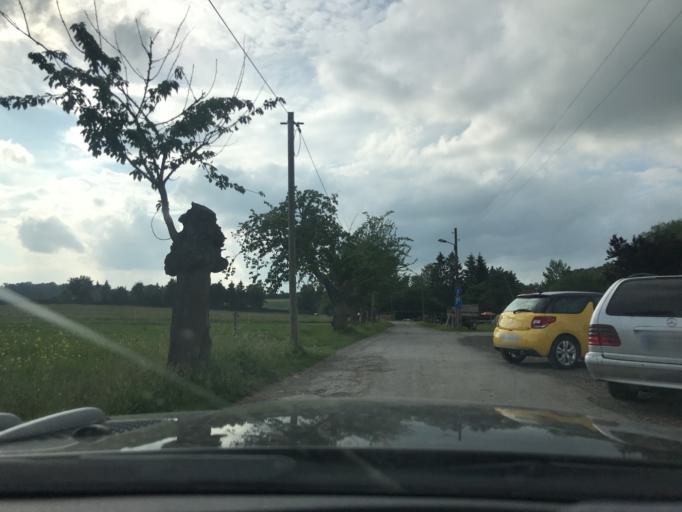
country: DE
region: Thuringia
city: Muehlhausen
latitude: 51.2084
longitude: 10.4220
